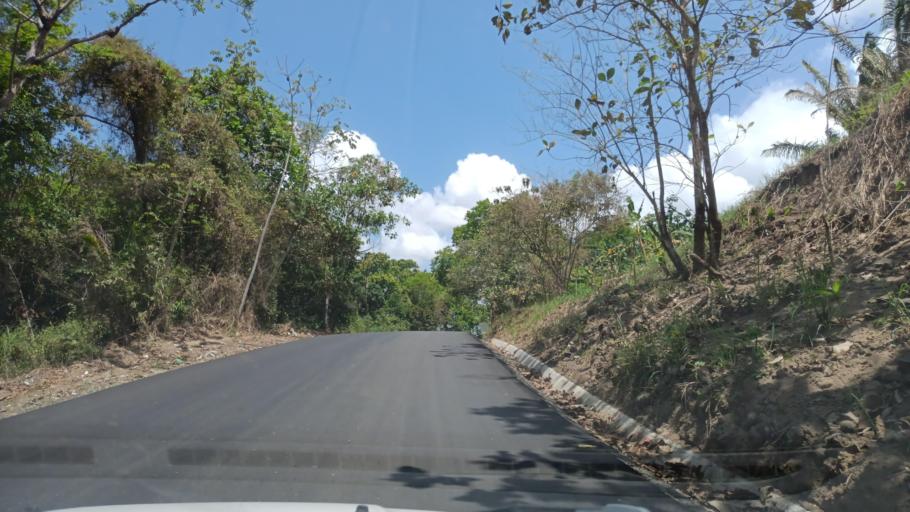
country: PA
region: Panama
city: Alcalde Diaz
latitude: 9.0945
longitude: -79.5764
